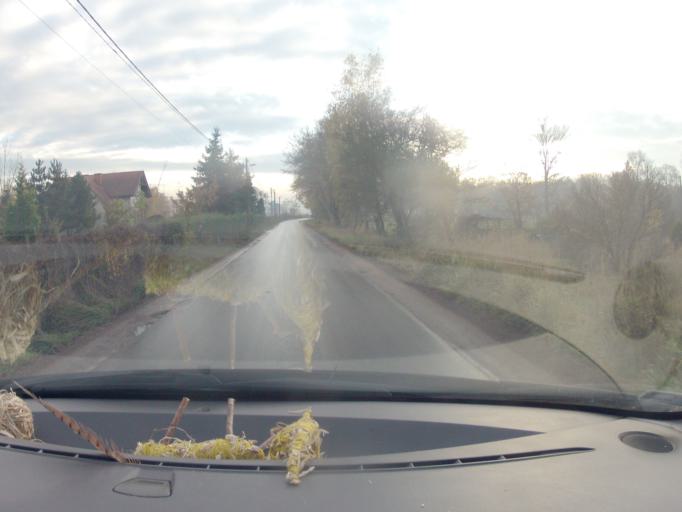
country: PL
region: Lesser Poland Voivodeship
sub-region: Krakow
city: Sidzina
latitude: 50.0039
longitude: 19.8893
